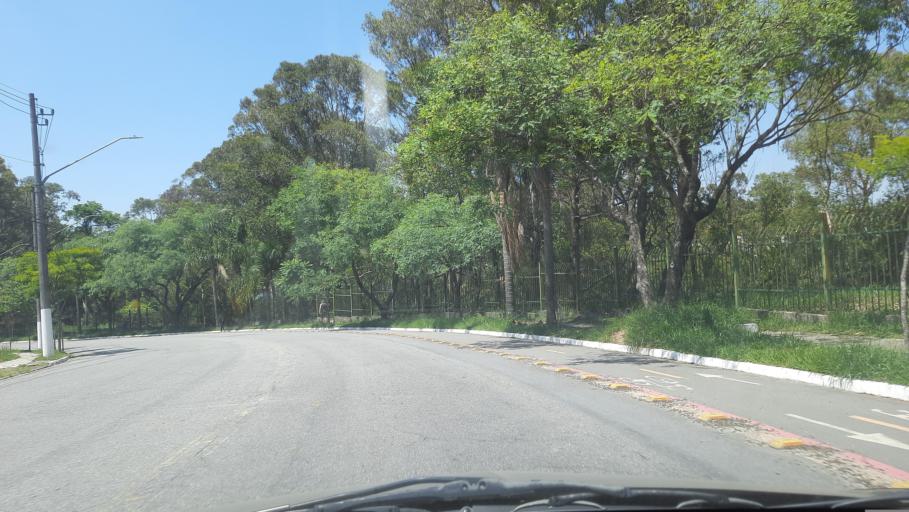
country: BR
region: Sao Paulo
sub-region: Caieiras
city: Caieiras
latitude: -23.4421
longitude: -46.7300
